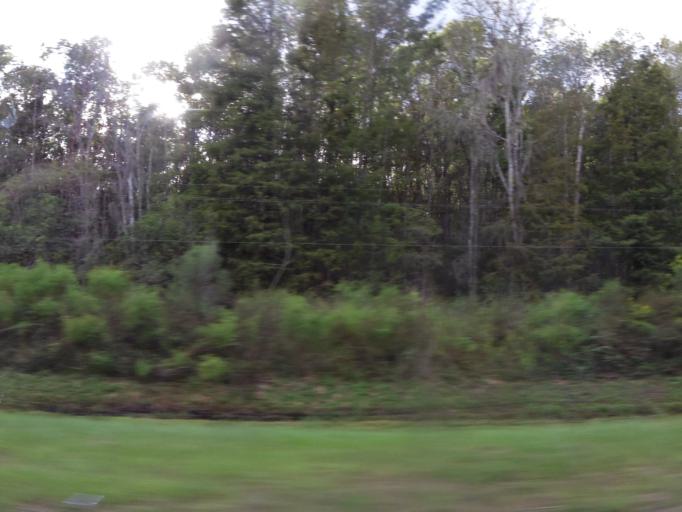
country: US
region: Georgia
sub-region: Liberty County
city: Midway
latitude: 31.8170
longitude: -81.4300
